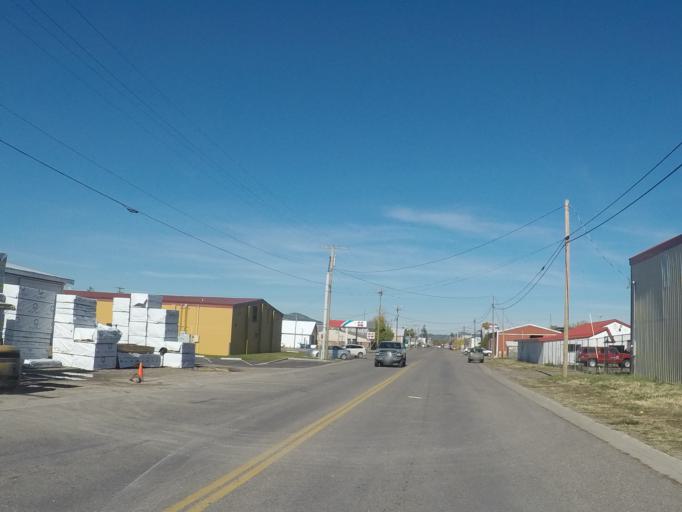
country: US
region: Montana
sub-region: Lake County
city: Polson
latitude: 47.6865
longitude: -114.1634
